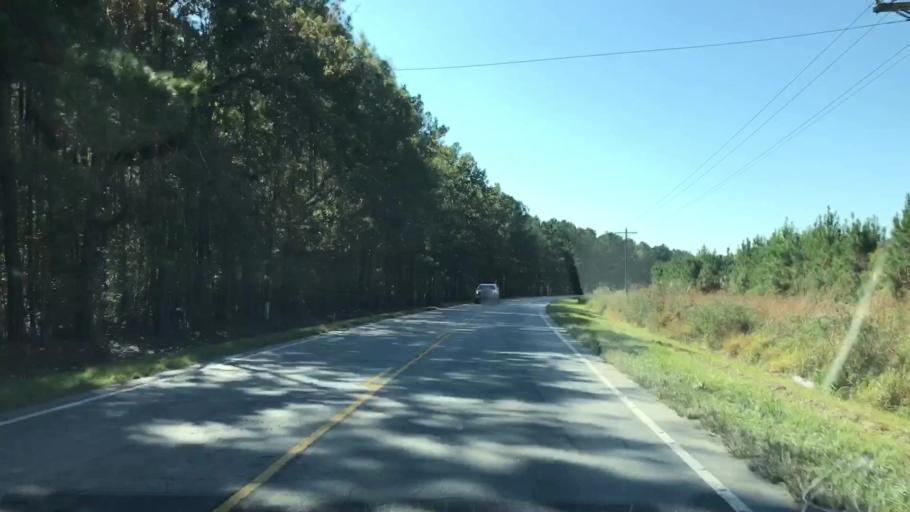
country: US
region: South Carolina
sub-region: Jasper County
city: Ridgeland
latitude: 32.4148
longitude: -80.9001
